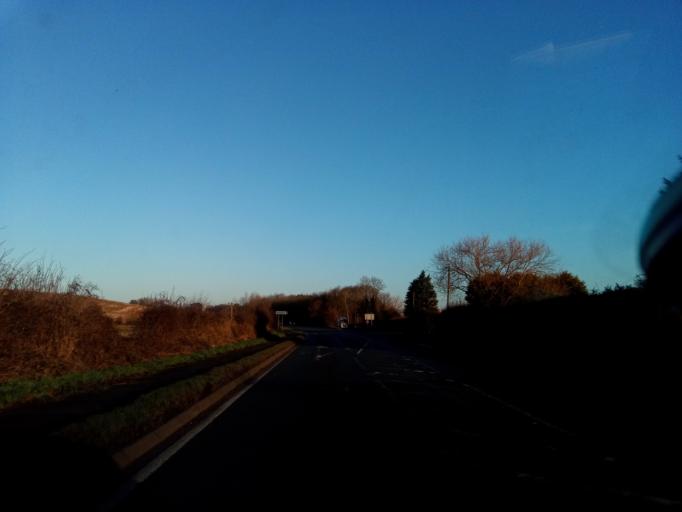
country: GB
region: England
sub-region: Leicestershire
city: Kegworth
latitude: 52.8245
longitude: -1.2720
